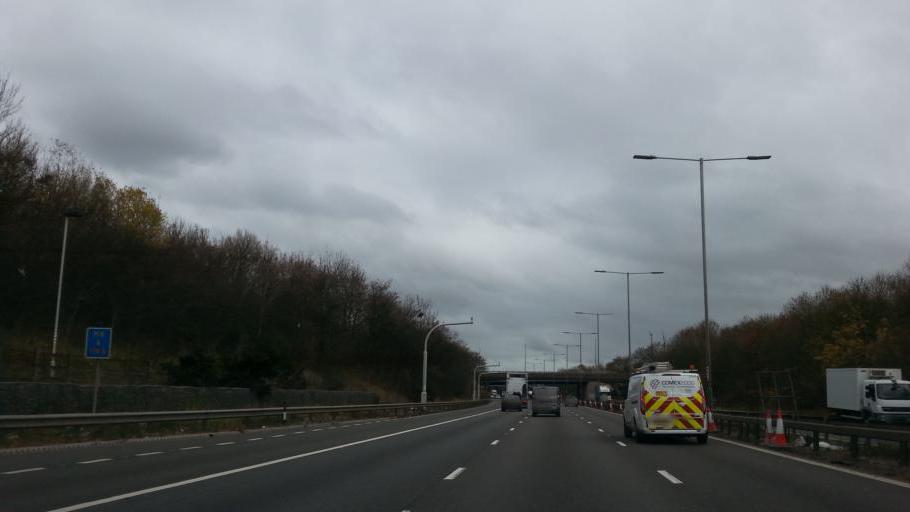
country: GB
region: England
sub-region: Warwickshire
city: Water Orton
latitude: 52.5051
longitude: -1.7420
